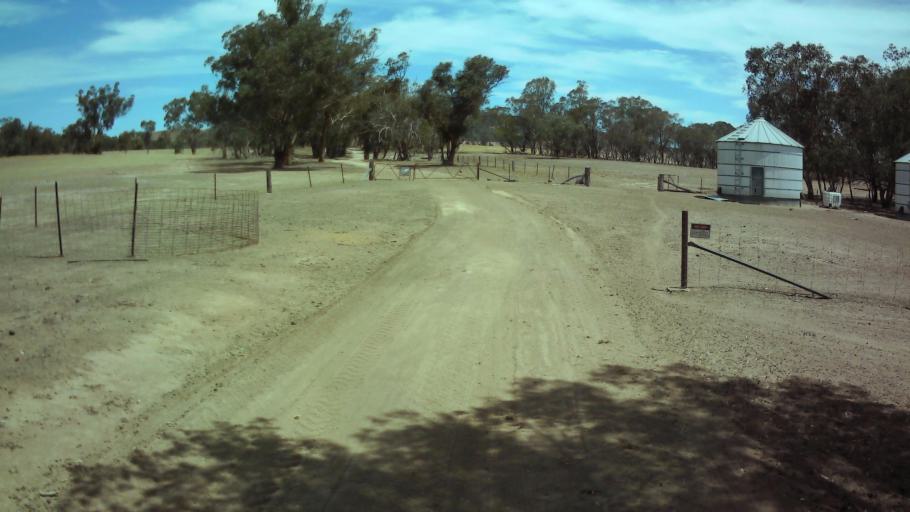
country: AU
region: New South Wales
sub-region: Weddin
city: Grenfell
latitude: -33.7777
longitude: 148.1515
